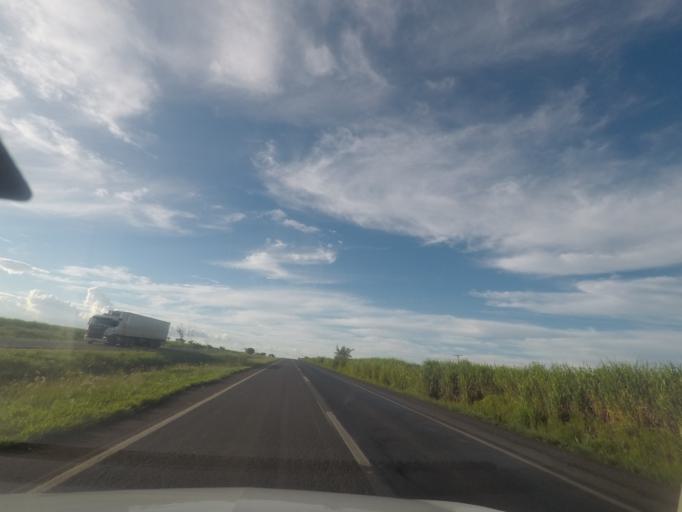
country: BR
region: Goias
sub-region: Itumbiara
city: Itumbiara
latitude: -18.2160
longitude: -49.2710
